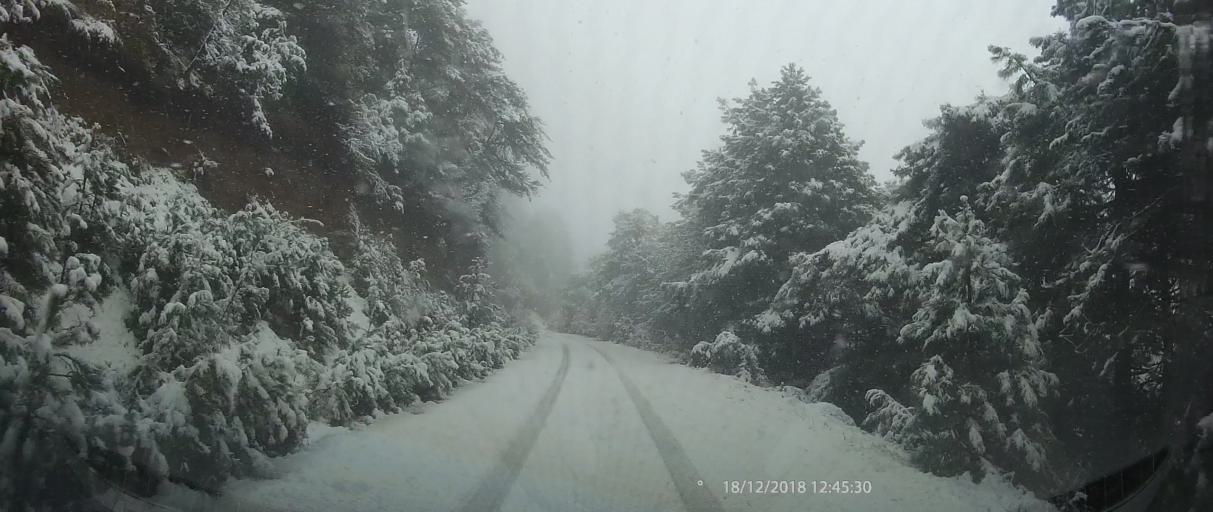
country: GR
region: Central Macedonia
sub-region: Nomos Pierias
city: Litochoro
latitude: 40.0987
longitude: 22.4299
